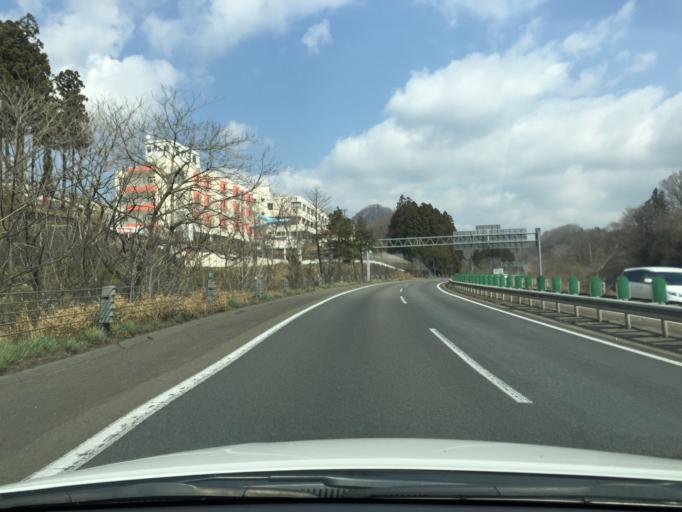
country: JP
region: Miyagi
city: Sendai
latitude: 38.2191
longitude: 140.8014
